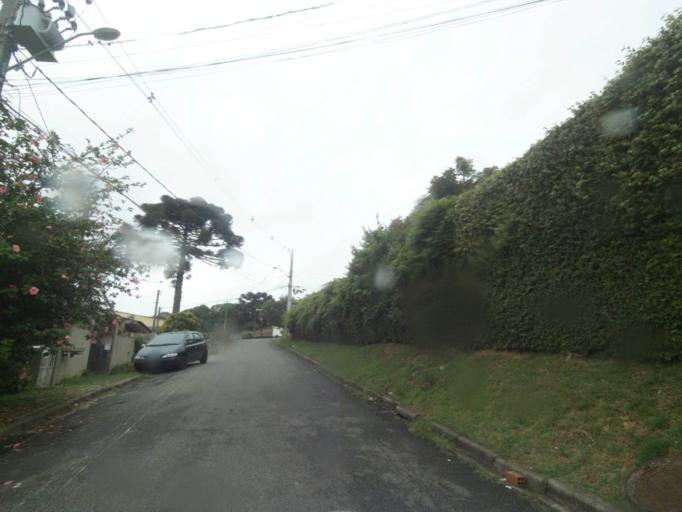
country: BR
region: Parana
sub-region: Curitiba
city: Curitiba
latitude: -25.4228
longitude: -49.3214
